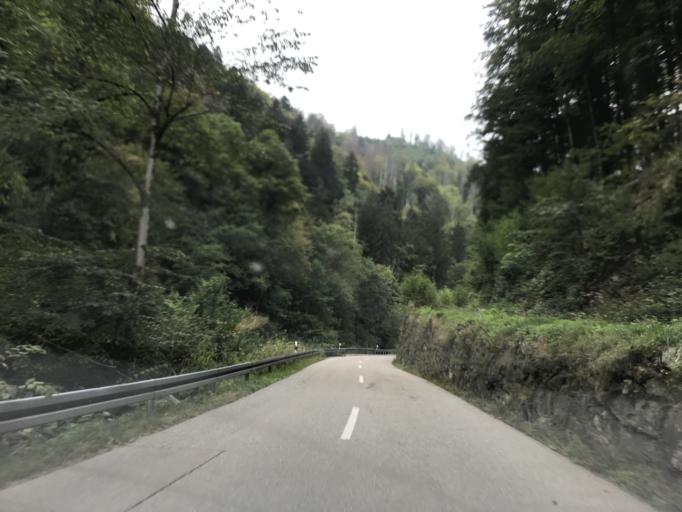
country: DE
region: Baden-Wuerttemberg
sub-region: Freiburg Region
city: Hasel
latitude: 47.6720
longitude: 7.9357
